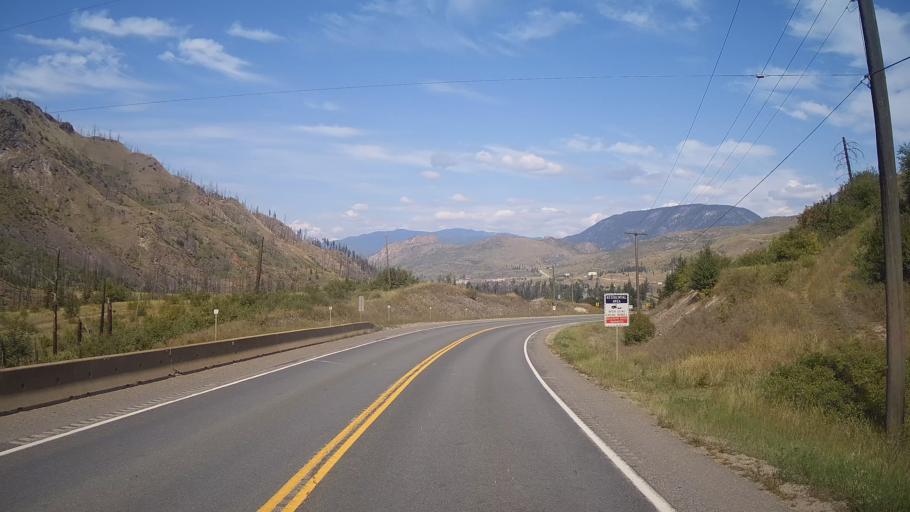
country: CA
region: British Columbia
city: Kamloops
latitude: 51.1107
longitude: -120.1364
